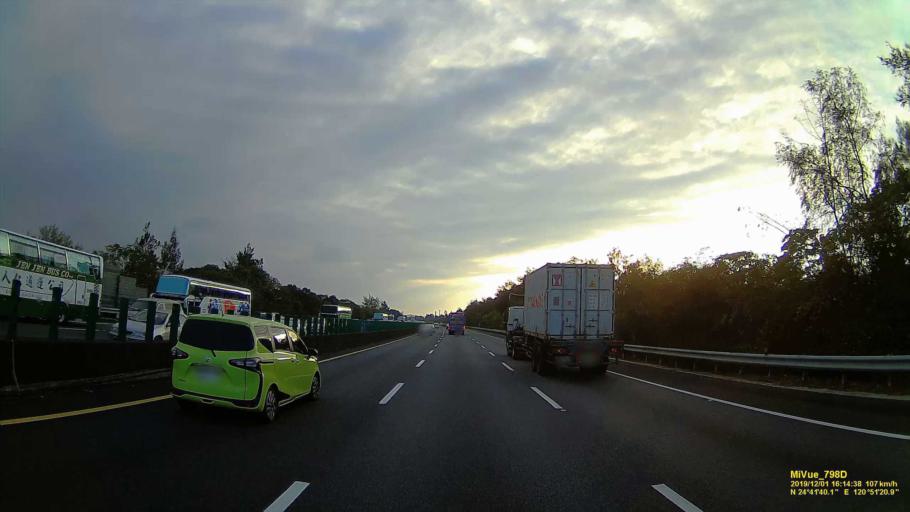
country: TW
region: Taiwan
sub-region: Miaoli
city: Miaoli
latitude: 24.6943
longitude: 120.8564
